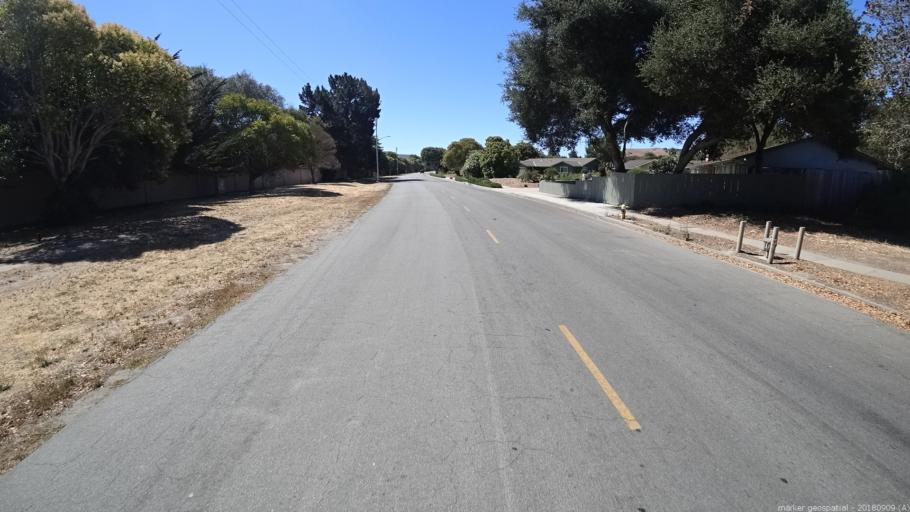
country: US
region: California
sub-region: Monterey County
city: Salinas
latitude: 36.6171
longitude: -121.6880
